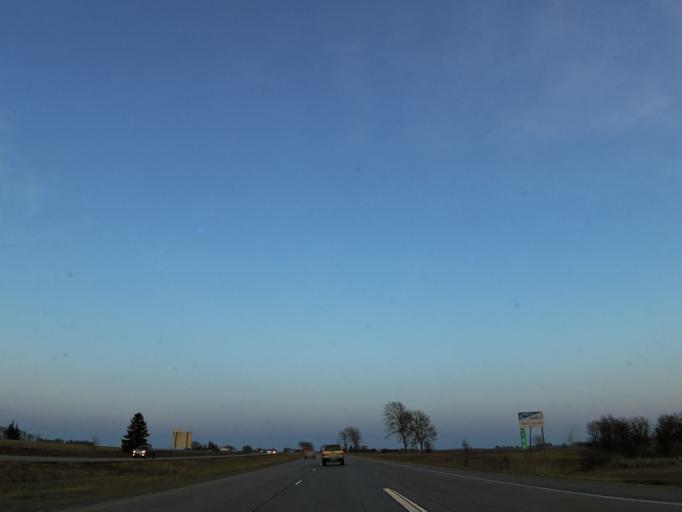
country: US
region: Minnesota
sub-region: Mower County
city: Austin
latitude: 43.6713
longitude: -92.8652
